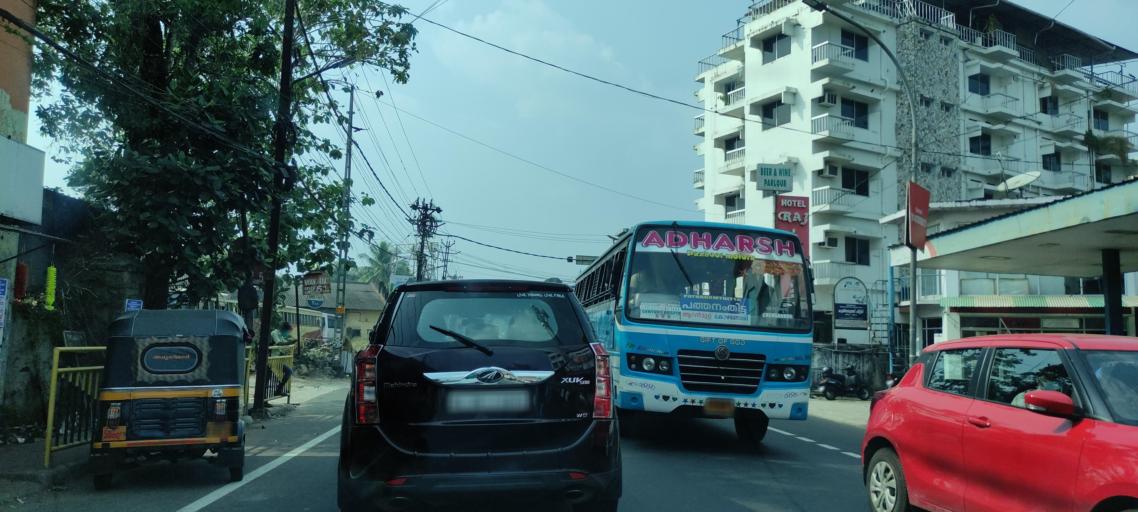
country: IN
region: Kerala
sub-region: Alappuzha
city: Chengannur
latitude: 9.3187
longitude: 76.6129
